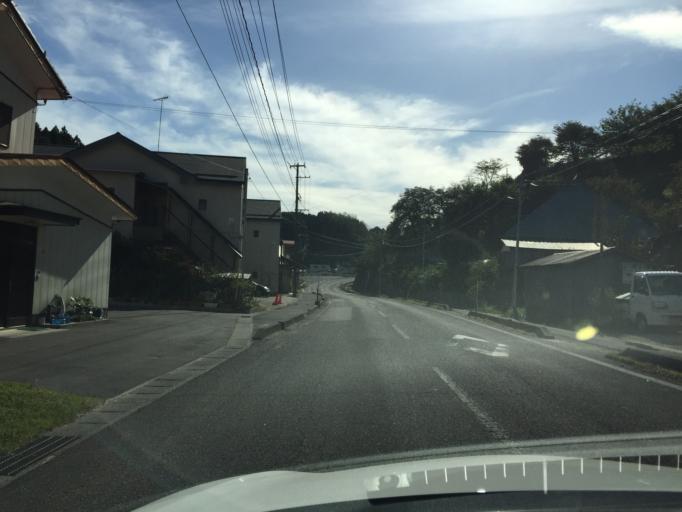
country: JP
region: Fukushima
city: Miharu
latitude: 37.4501
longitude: 140.4874
